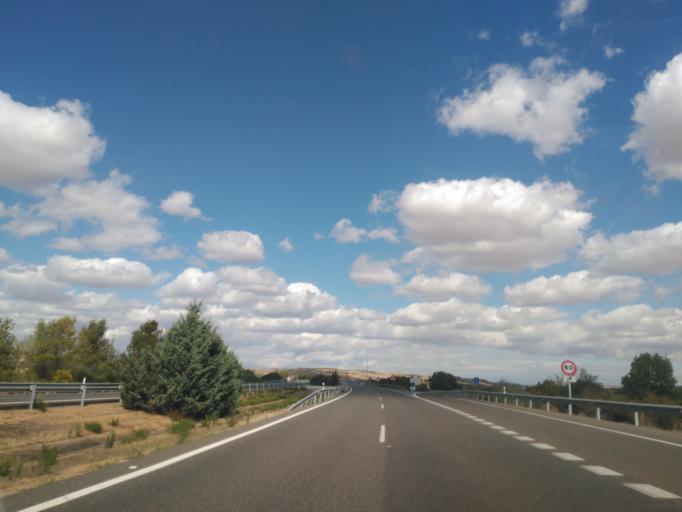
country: ES
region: Castille and Leon
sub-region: Provincia de Palencia
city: Soto de Cerrato
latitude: 41.9793
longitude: -4.4373
